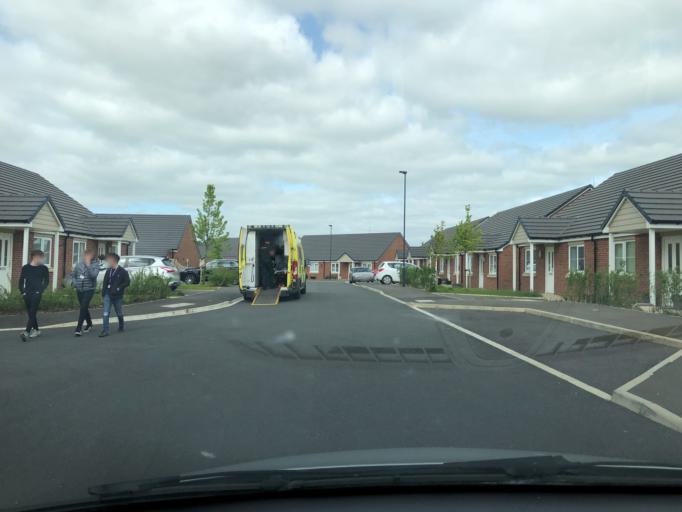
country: GB
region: England
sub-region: North Yorkshire
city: Thirsk
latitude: 54.2199
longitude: -1.3497
